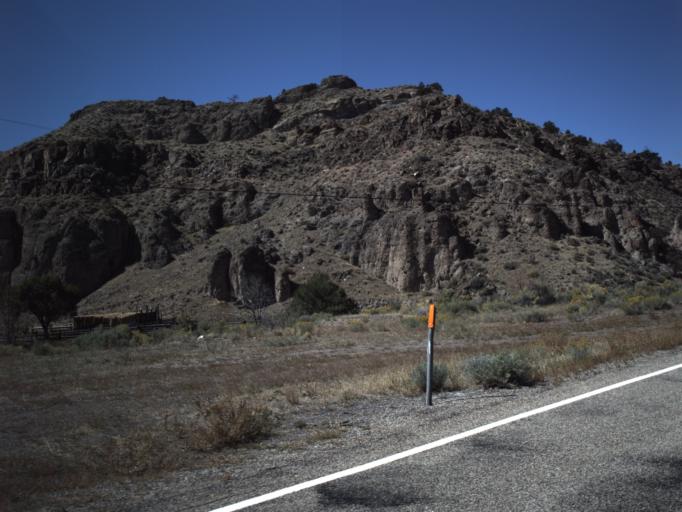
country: US
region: Utah
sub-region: Piute County
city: Junction
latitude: 38.1979
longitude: -112.1506
